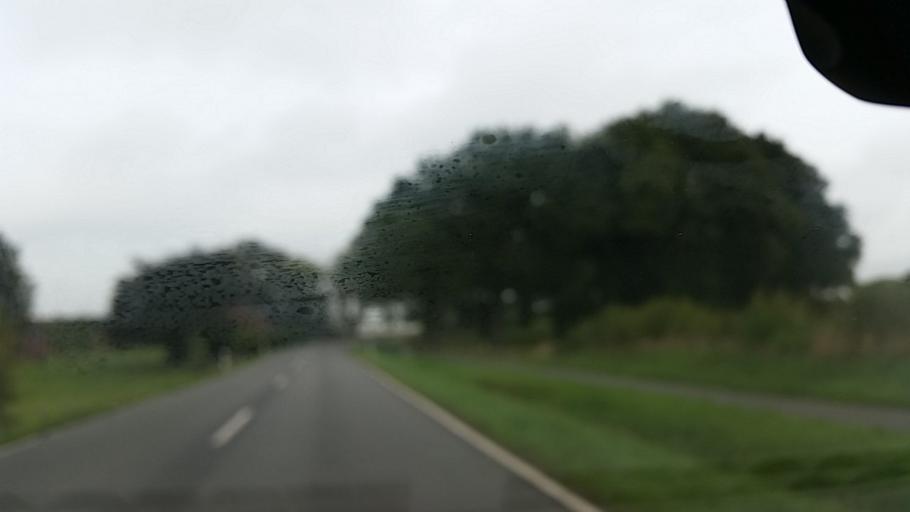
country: DE
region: Schleswig-Holstein
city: Schmalfeld
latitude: 53.8618
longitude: 9.9743
